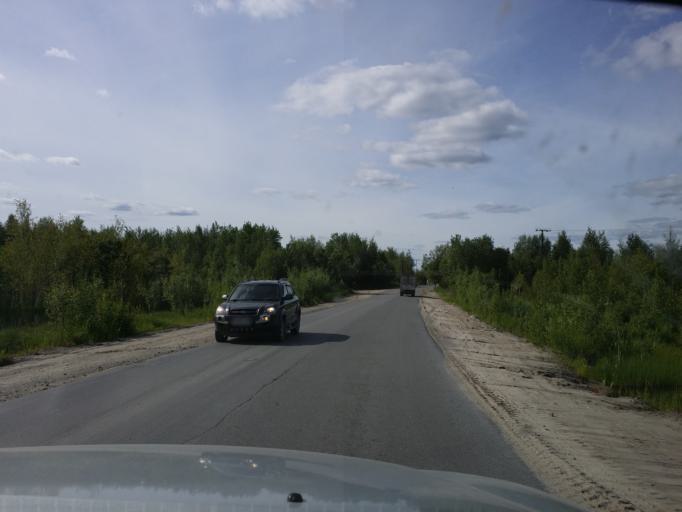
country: RU
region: Khanty-Mansiyskiy Avtonomnyy Okrug
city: Nizhnevartovsk
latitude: 60.9994
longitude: 76.5629
